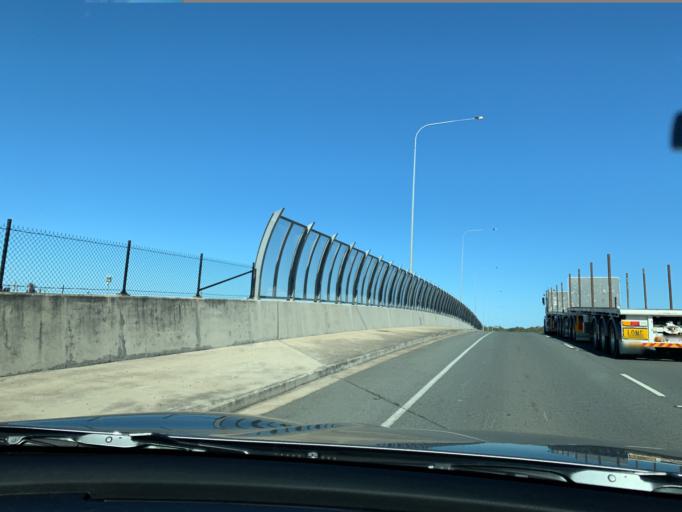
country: AU
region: Queensland
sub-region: Brisbane
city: Wynnum
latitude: -27.4245
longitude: 153.1470
